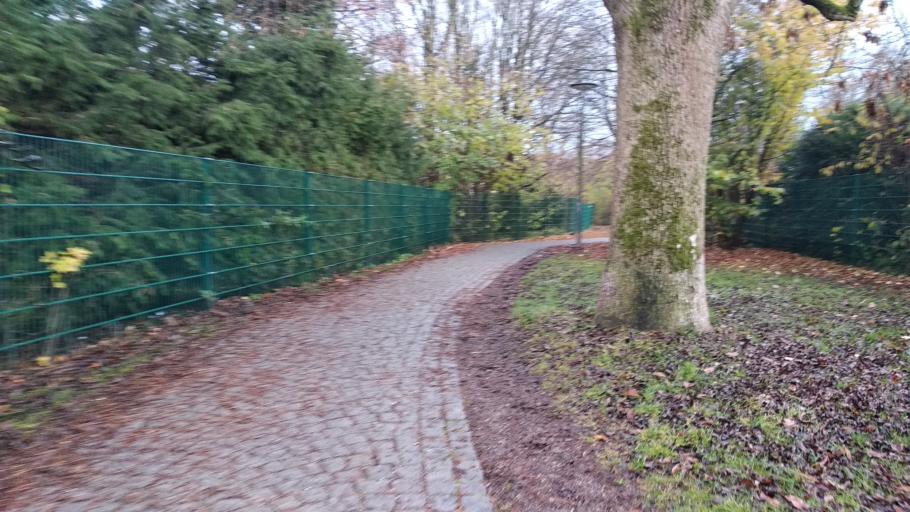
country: DE
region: Bavaria
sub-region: Upper Bavaria
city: Neubiberg
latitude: 48.1015
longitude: 11.6331
